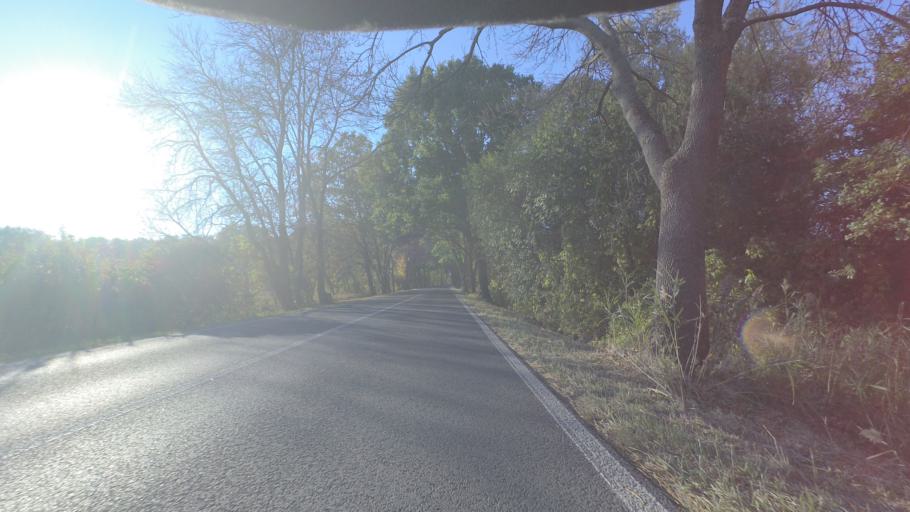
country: DE
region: Brandenburg
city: Zossen
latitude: 52.2534
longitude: 13.4656
